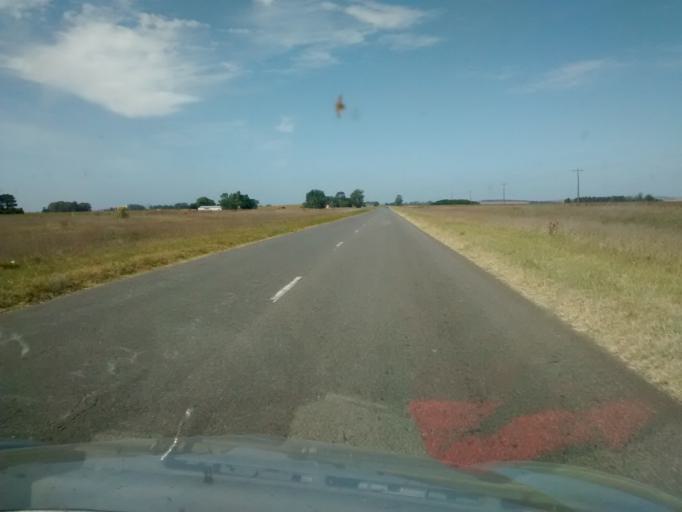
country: AR
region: Buenos Aires
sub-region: Partido de Balcarce
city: Balcarce
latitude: -37.6480
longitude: -58.4838
